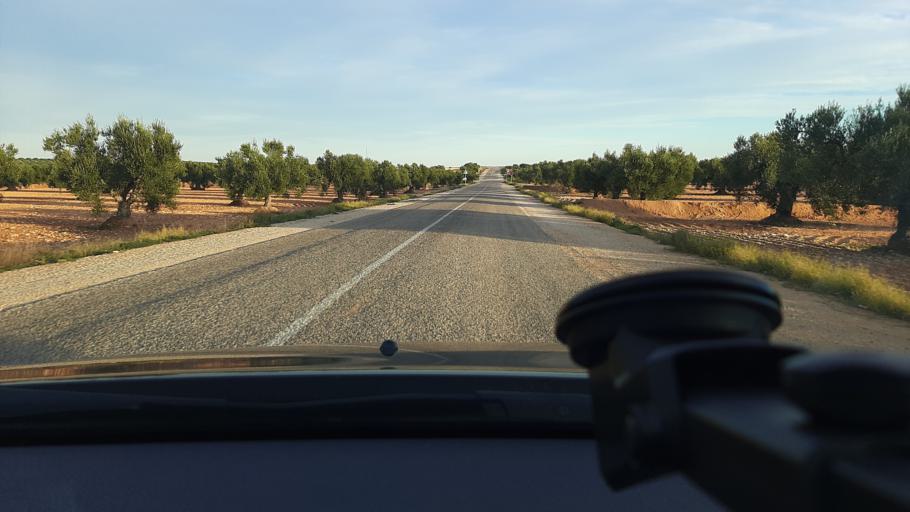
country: TN
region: Safaqis
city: Sfax
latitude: 34.9571
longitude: 10.5427
